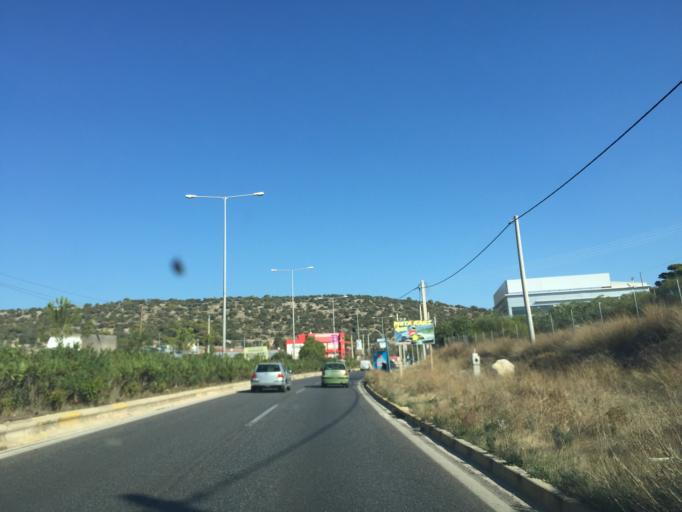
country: GR
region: Attica
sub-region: Nomarchia Anatolikis Attikis
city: Kitsi
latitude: 37.8545
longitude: 23.8312
